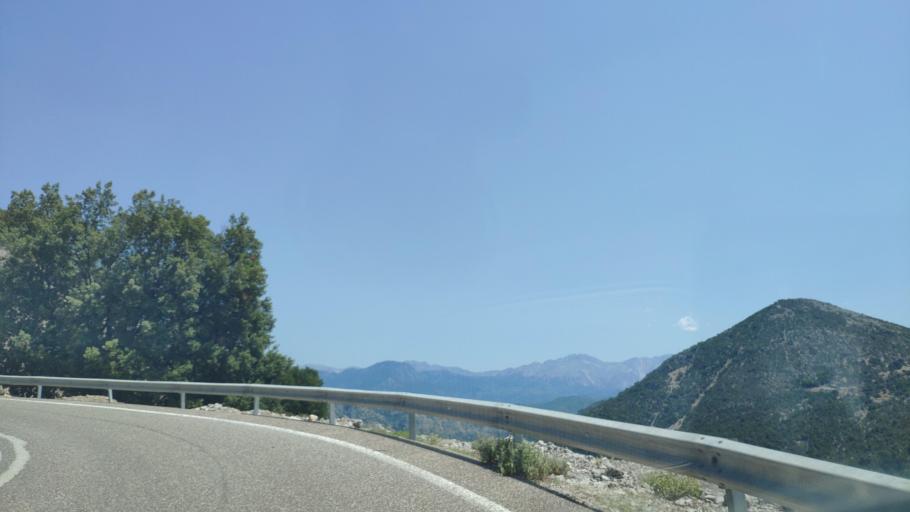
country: GR
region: West Greece
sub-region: Nomos Aitolias kai Akarnanias
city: Krikellos
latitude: 39.0214
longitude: 21.3700
